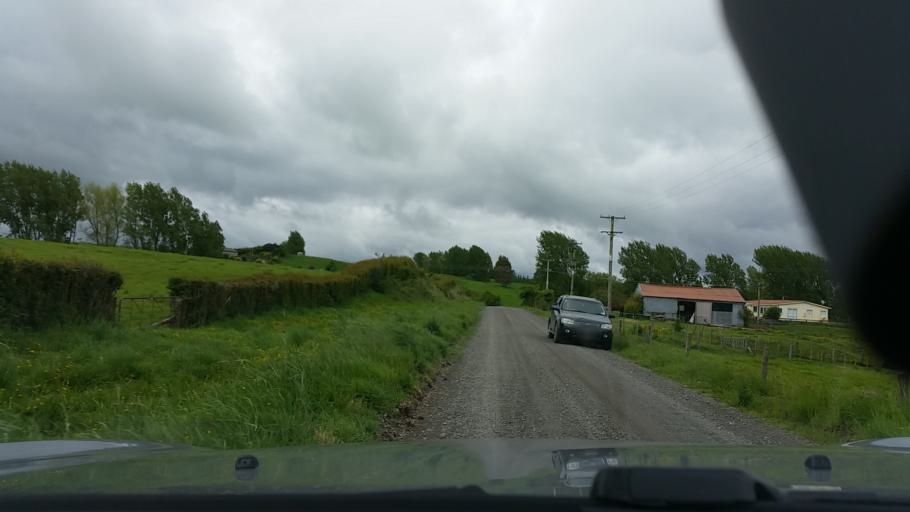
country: NZ
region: Bay of Plenty
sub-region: Whakatane District
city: Murupara
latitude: -38.3091
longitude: 176.4689
